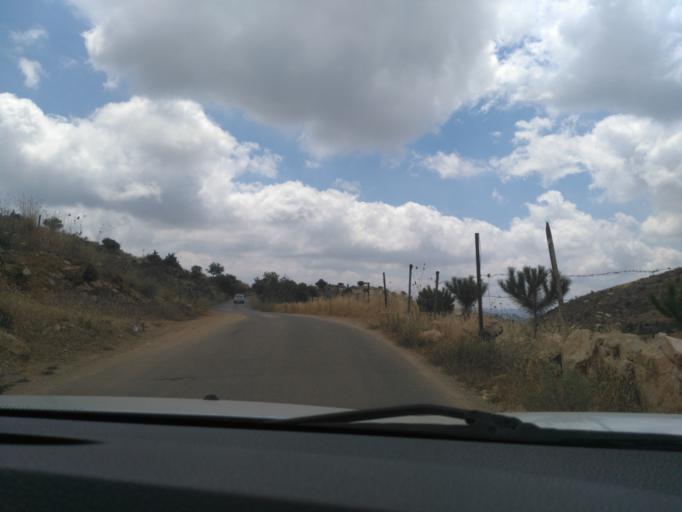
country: LB
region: Mont-Liban
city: Beit ed Dine
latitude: 33.6823
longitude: 35.6647
